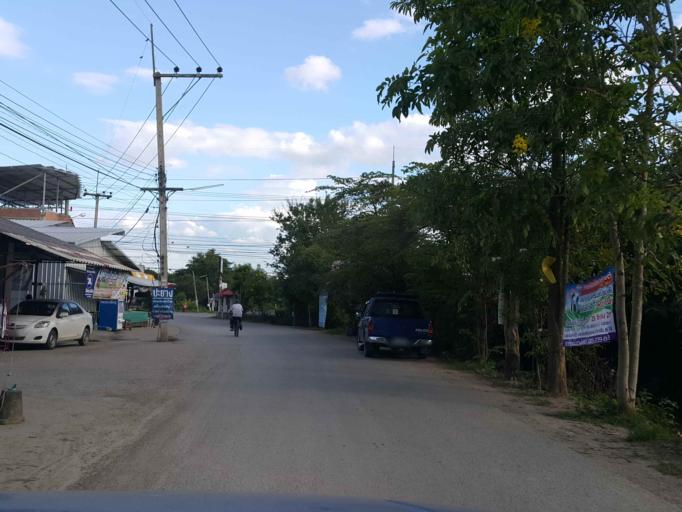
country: TH
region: Chiang Mai
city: San Sai
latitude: 18.9183
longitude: 98.9749
